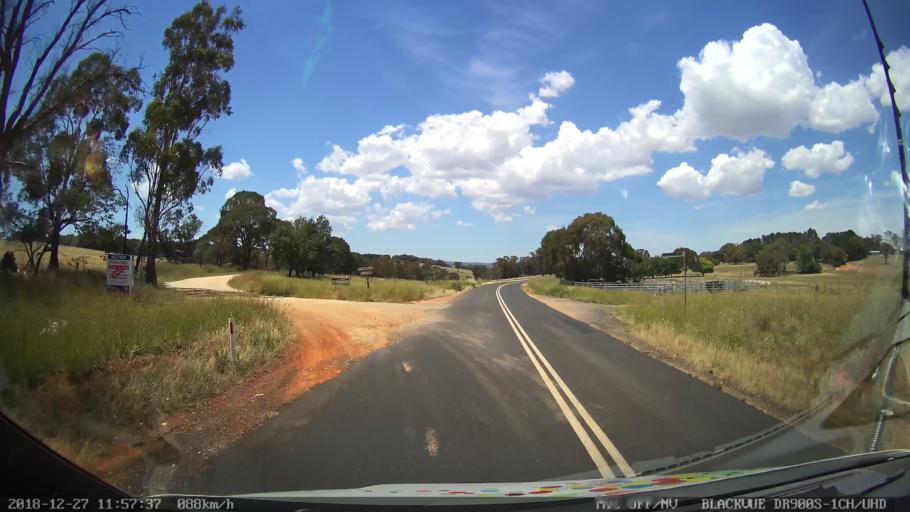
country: AU
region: New South Wales
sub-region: Blayney
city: Blayney
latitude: -33.7139
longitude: 149.3879
